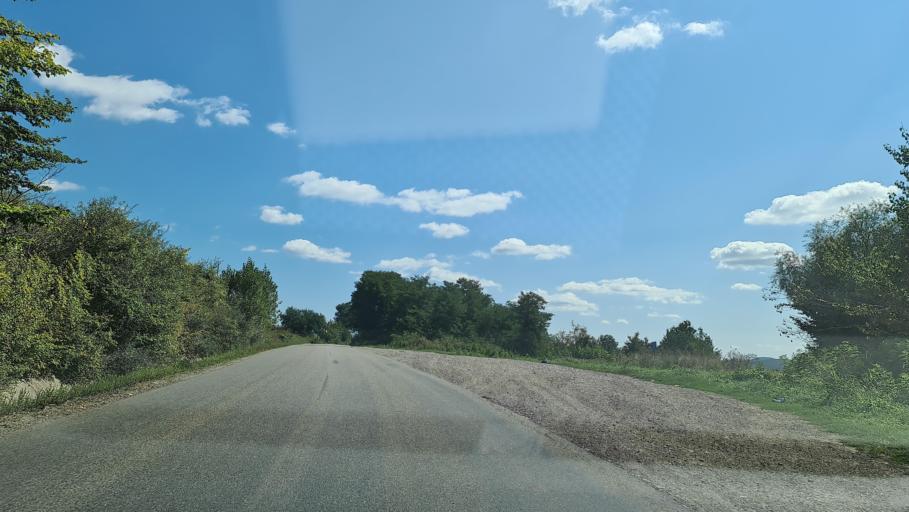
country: RO
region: Bacau
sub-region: Comuna Beresti-Tazlau
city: Beresti-Tazlau
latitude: 46.4957
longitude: 26.6828
